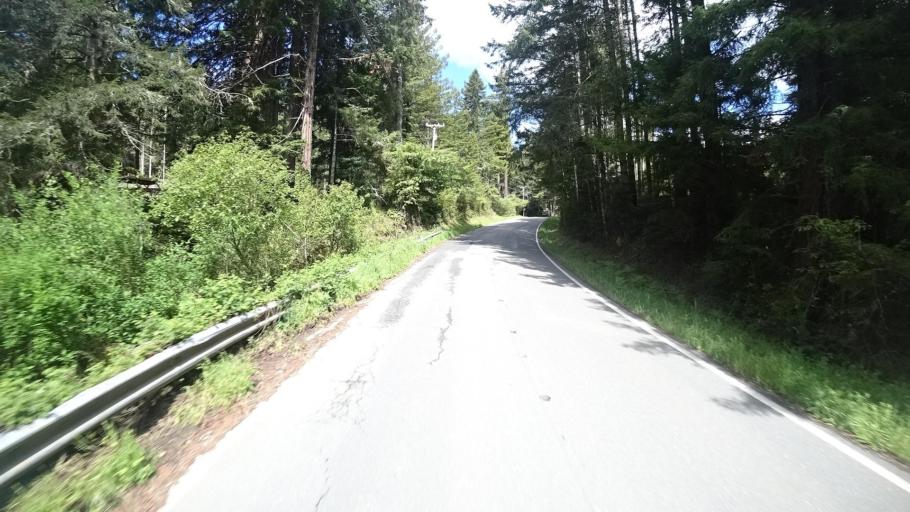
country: US
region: California
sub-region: Humboldt County
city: Blue Lake
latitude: 40.9402
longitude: -124.0240
